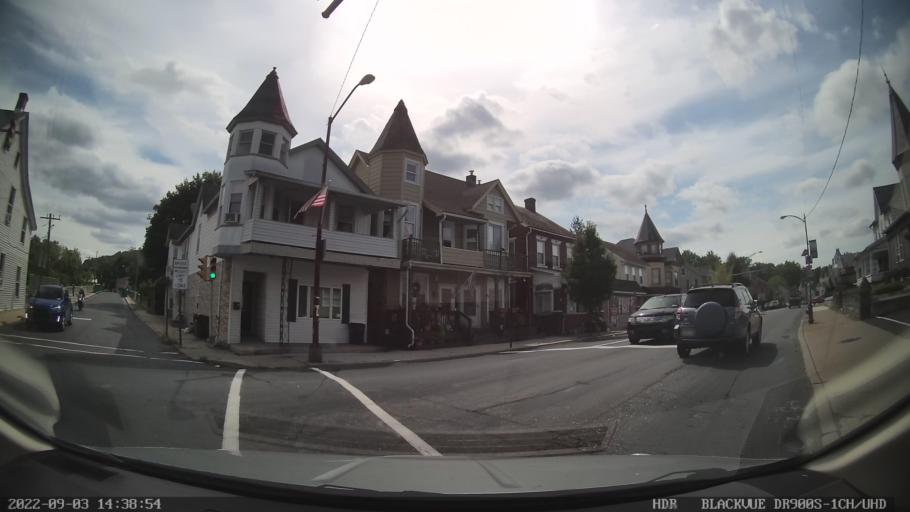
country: US
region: Pennsylvania
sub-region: Northampton County
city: Walnutport
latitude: 40.7527
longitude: -75.6059
